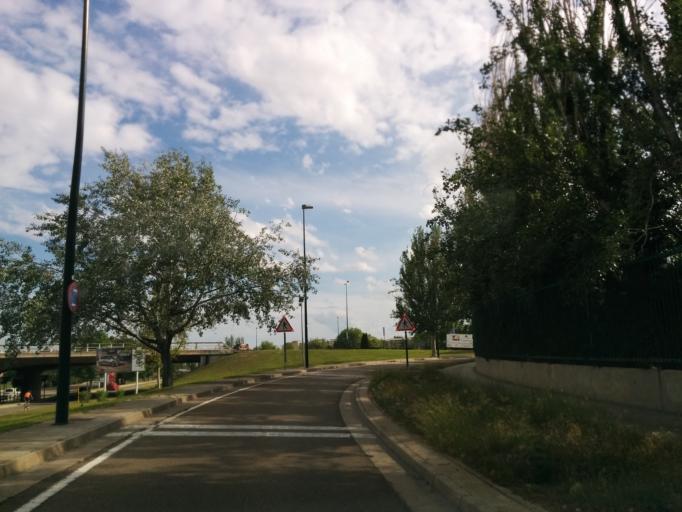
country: ES
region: Aragon
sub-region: Provincia de Zaragoza
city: Zaragoza
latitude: 41.6741
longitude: -0.8813
